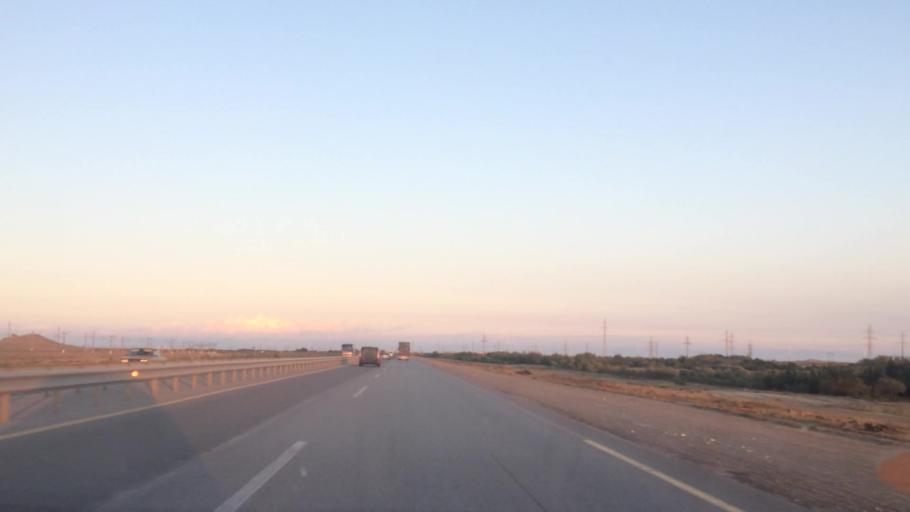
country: AZ
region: Baki
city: Qobustan
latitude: 39.9460
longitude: 49.3463
